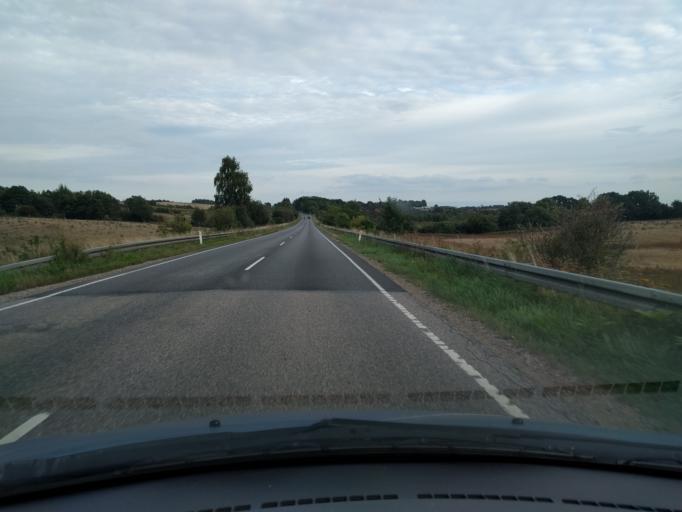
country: DK
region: Zealand
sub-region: Vordingborg Kommune
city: Nyrad
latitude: 55.0071
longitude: 11.9790
